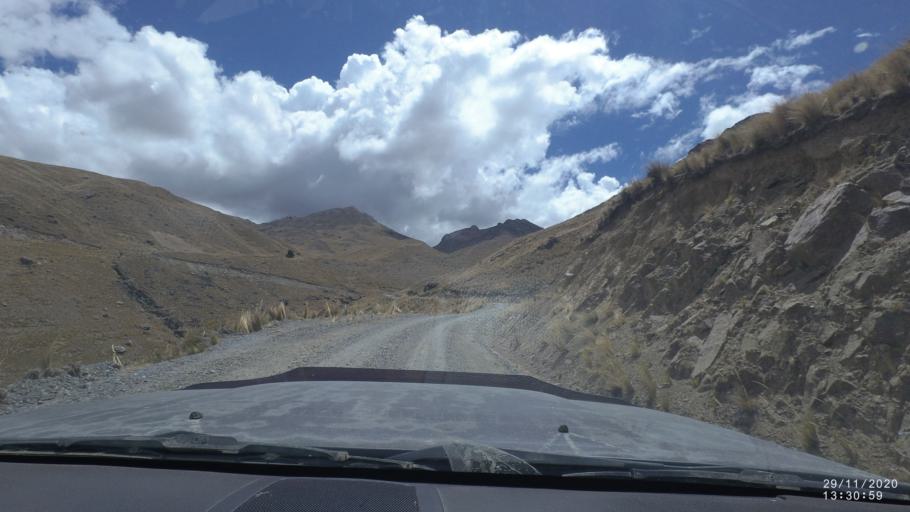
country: BO
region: Cochabamba
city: Cochabamba
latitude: -17.1035
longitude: -66.3419
